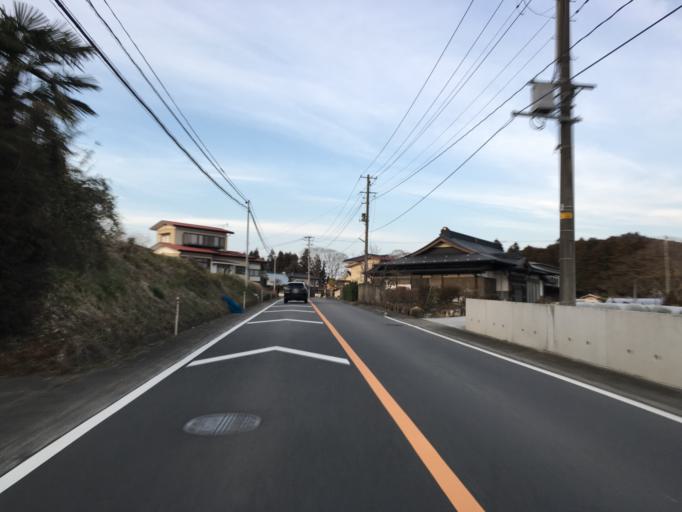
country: JP
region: Ibaraki
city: Daigo
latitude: 36.9489
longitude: 140.4082
